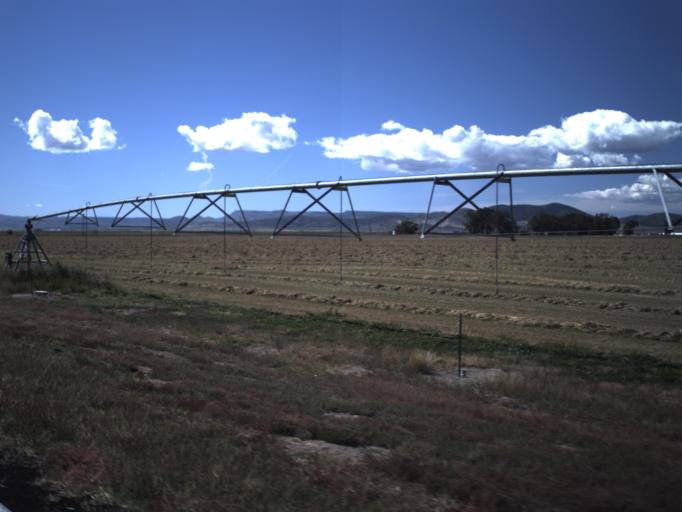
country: US
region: Utah
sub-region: Washington County
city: Enterprise
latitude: 37.6965
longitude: -113.6565
